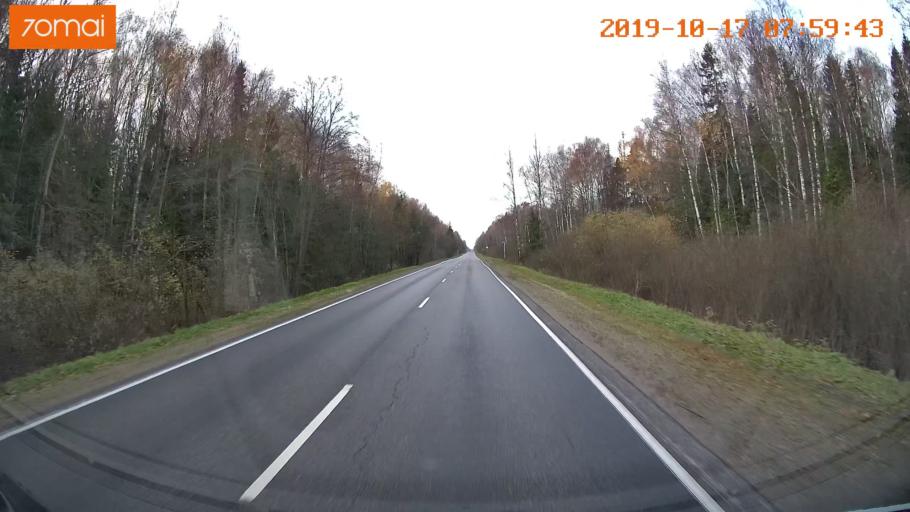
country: RU
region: Vladimir
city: Bavleny
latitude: 56.3907
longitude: 39.5331
